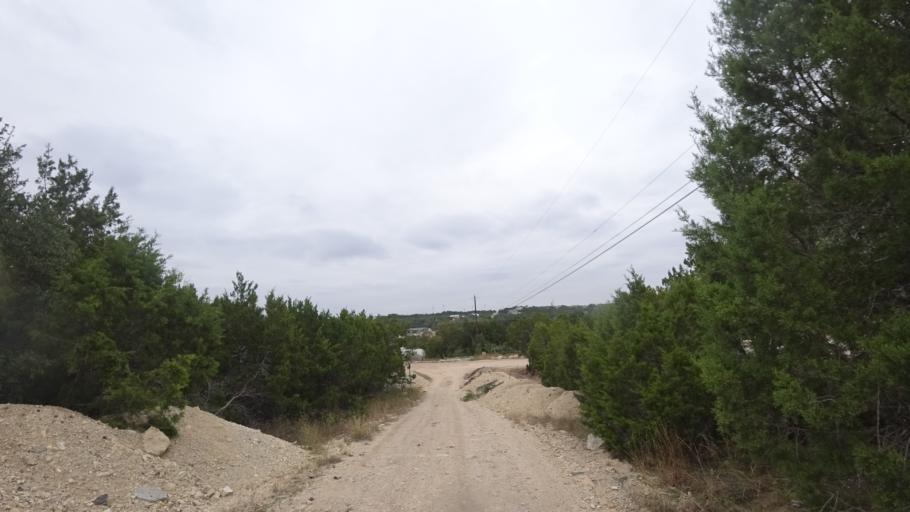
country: US
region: Texas
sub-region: Travis County
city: Hudson Bend
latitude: 30.3828
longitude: -97.9363
